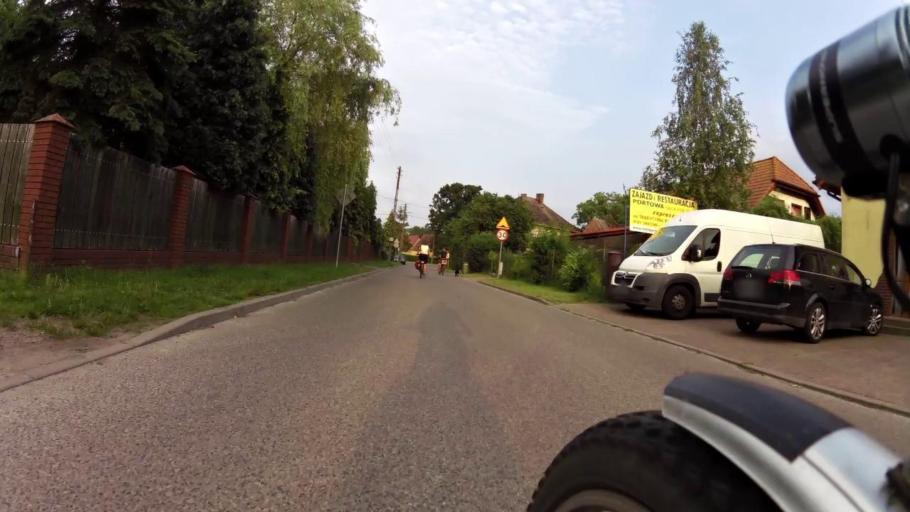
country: PL
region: West Pomeranian Voivodeship
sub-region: Powiat goleniowski
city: Stepnica
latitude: 53.6624
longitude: 14.4986
